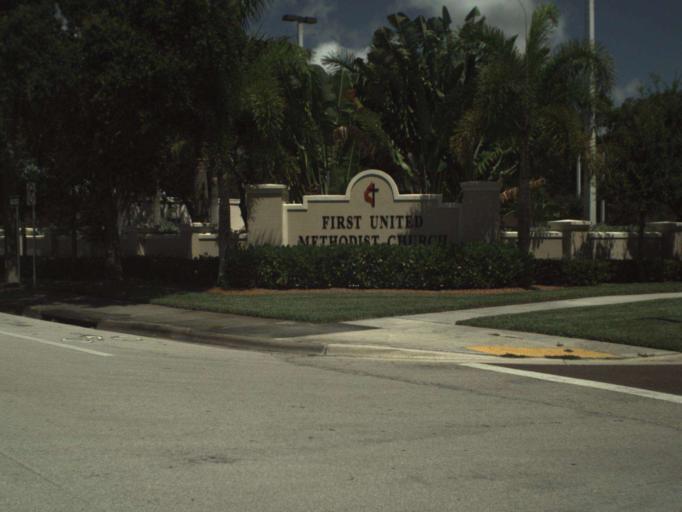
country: US
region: Florida
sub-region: Indian River County
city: Vero Beach
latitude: 27.6387
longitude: -80.4034
